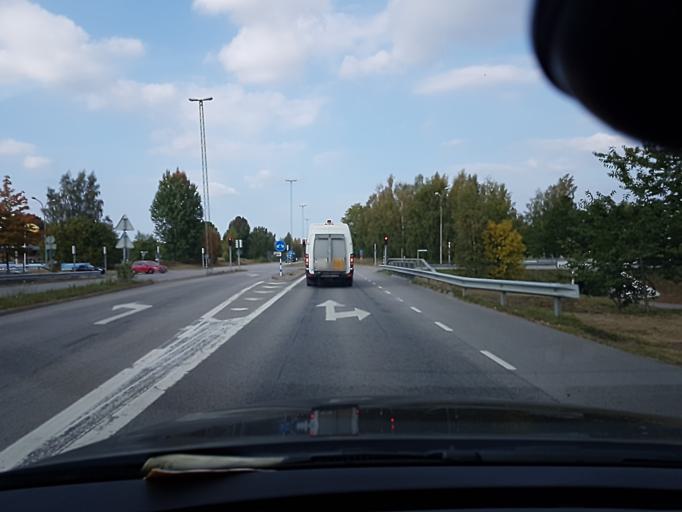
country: SE
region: Kronoberg
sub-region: Vaxjo Kommun
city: Vaexjoe
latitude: 56.8539
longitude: 14.8224
